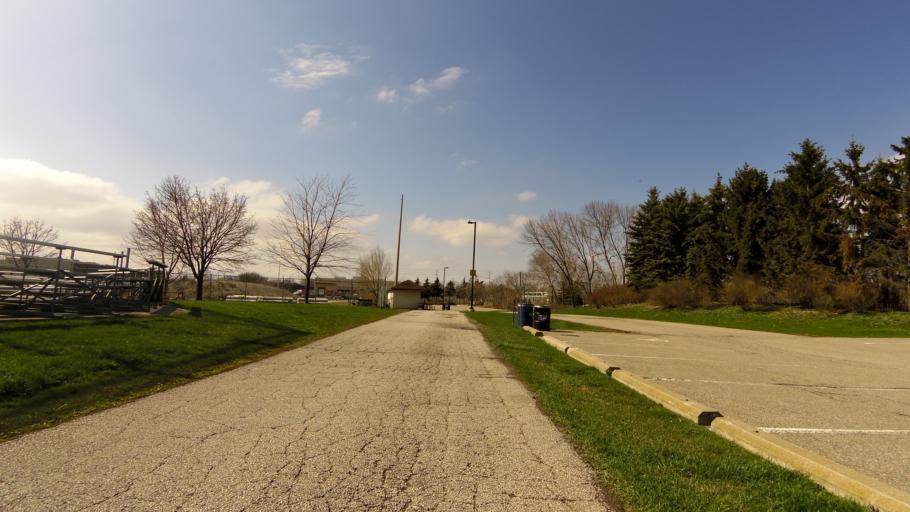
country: CA
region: Ontario
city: Etobicoke
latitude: 43.5714
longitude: -79.5569
